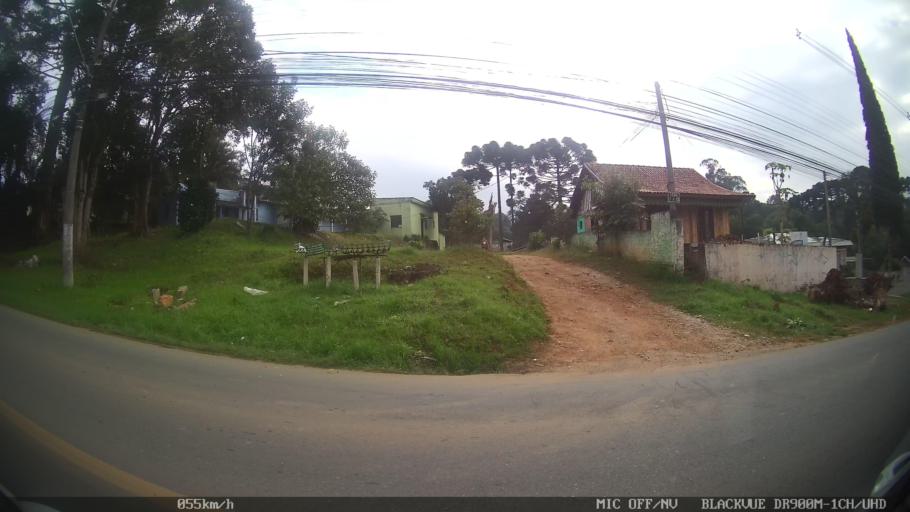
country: BR
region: Parana
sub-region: Curitiba
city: Curitiba
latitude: -25.3928
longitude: -49.3318
